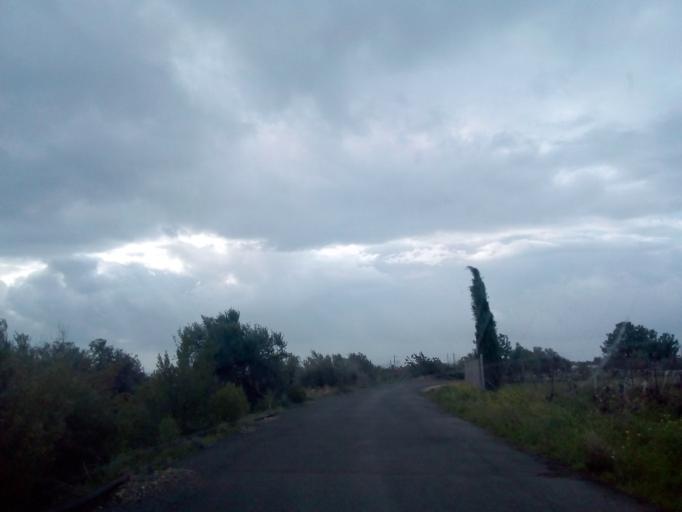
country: CY
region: Limassol
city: Ypsonas
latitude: 34.6755
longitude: 32.9651
